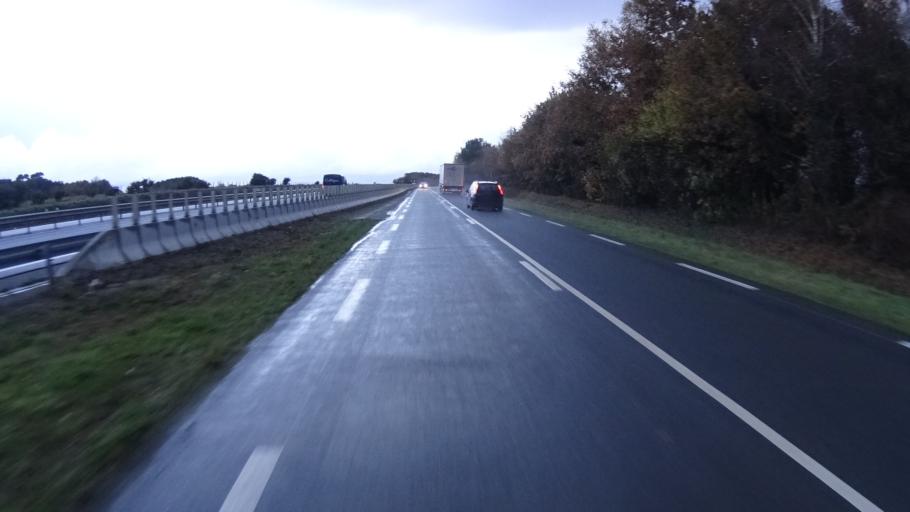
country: FR
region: Brittany
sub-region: Departement d'Ille-et-Vilaine
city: Bains-sur-Oust
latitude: 47.6946
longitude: -2.0421
